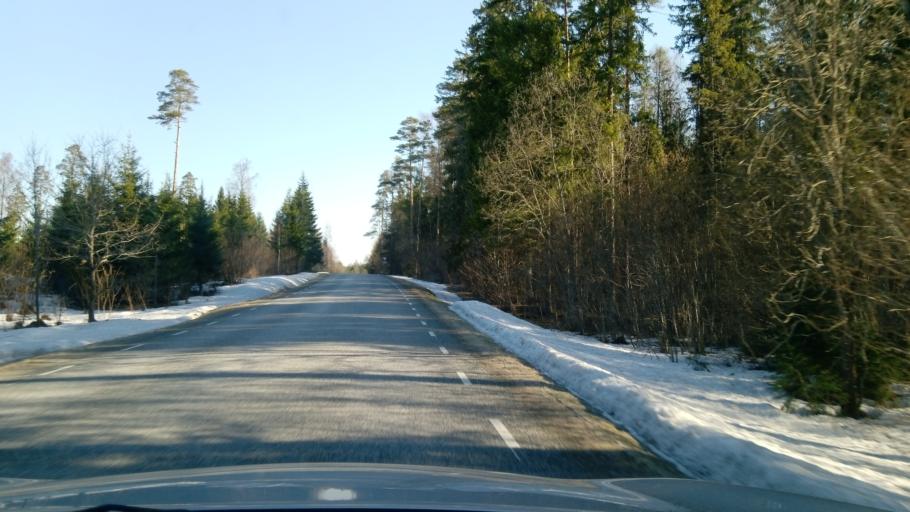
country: EE
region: Laeaene-Virumaa
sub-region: Tamsalu vald
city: Tamsalu
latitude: 59.2371
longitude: 26.1736
